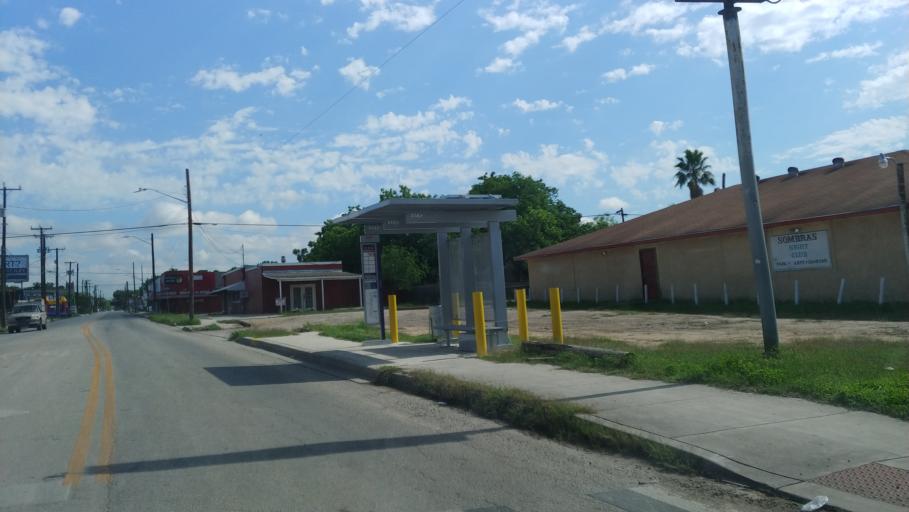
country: US
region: Texas
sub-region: Bexar County
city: San Antonio
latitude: 29.4496
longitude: -98.5244
